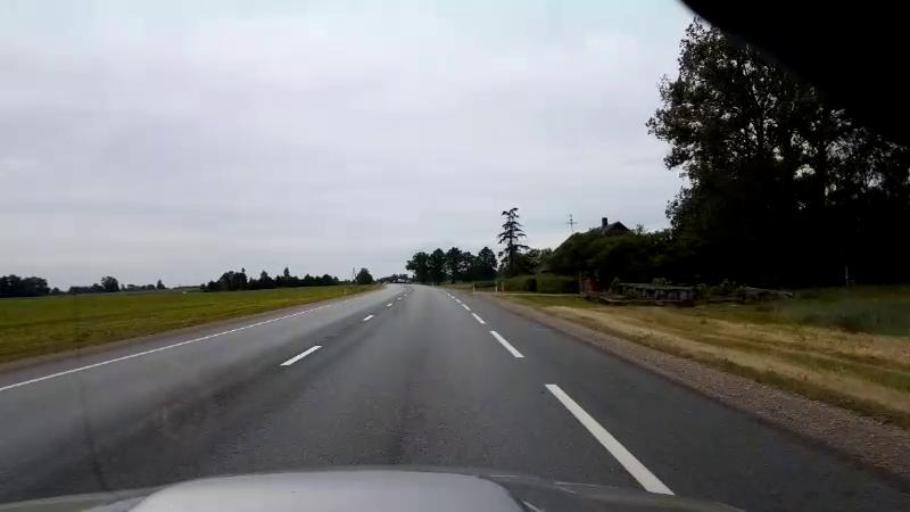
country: LV
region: Lecava
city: Iecava
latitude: 56.5746
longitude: 24.1771
